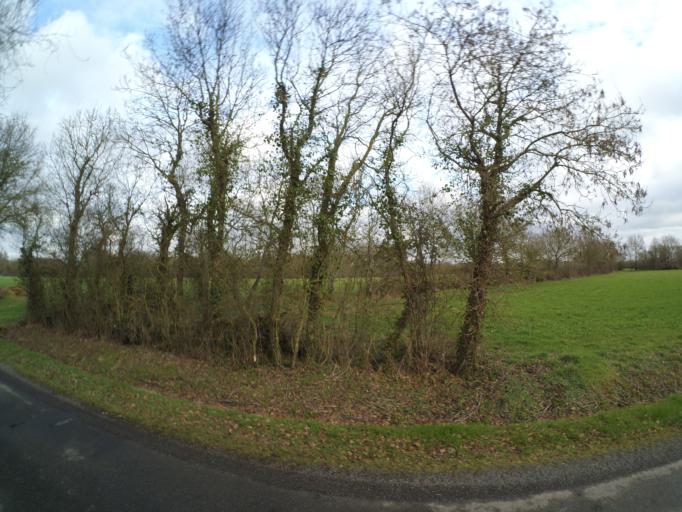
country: FR
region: Pays de la Loire
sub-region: Departement de la Vendee
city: La Bernardiere
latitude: 47.0347
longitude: -1.2927
